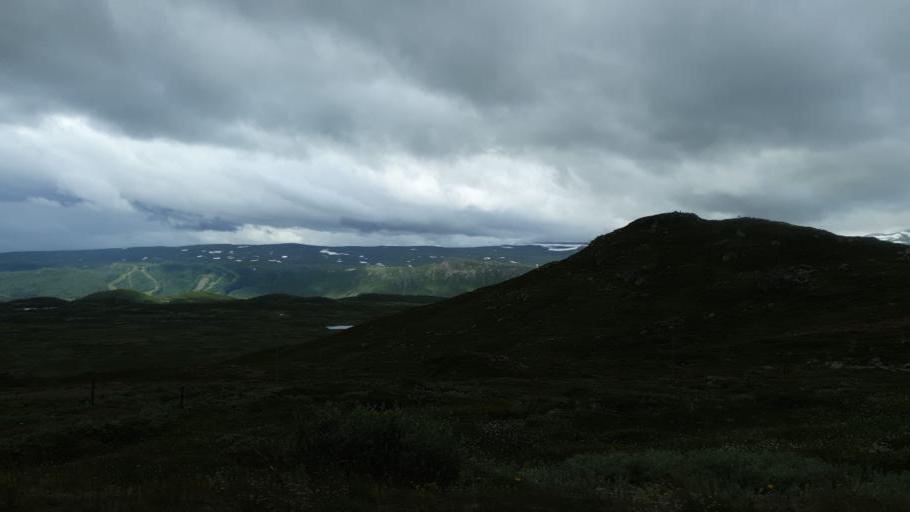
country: NO
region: Oppland
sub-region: Vestre Slidre
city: Slidre
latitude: 61.2819
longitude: 8.8372
